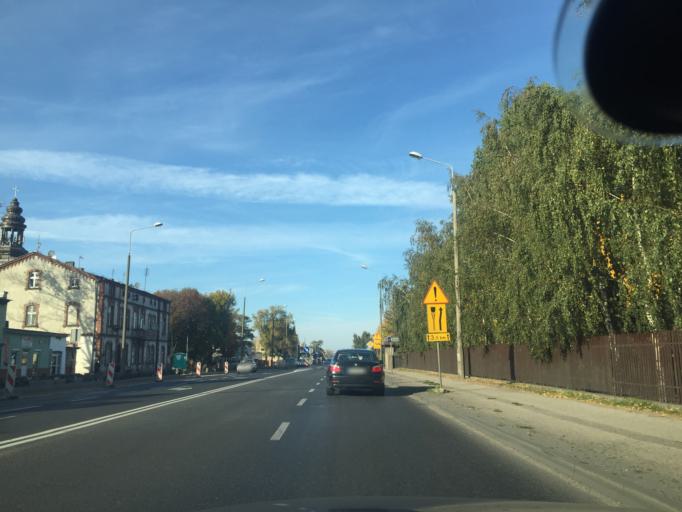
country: PL
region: Kujawsko-Pomorskie
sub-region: Powiat inowroclawski
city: Inowroclaw
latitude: 52.7539
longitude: 18.2563
